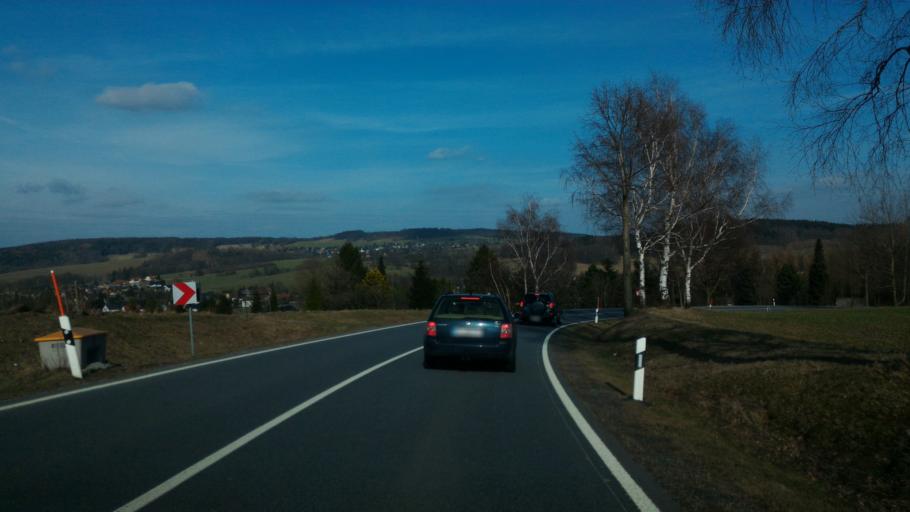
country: DE
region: Saxony
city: Steinigtwolmsdorf
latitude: 51.0616
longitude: 14.3360
